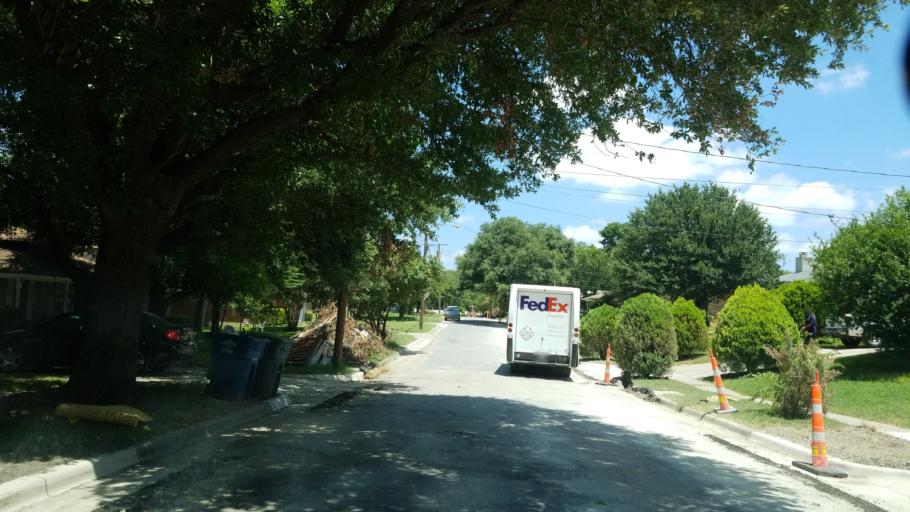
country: US
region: Texas
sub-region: Dallas County
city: Balch Springs
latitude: 32.7504
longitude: -96.6967
